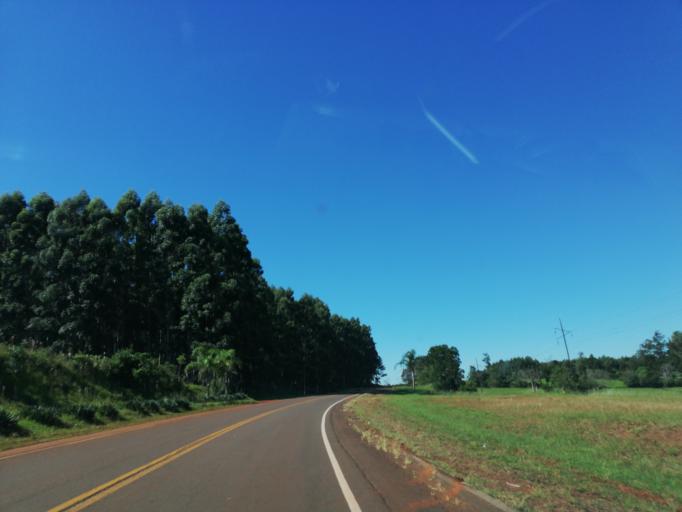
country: AR
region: Misiones
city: Dos de Mayo
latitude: -27.0711
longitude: -54.4084
